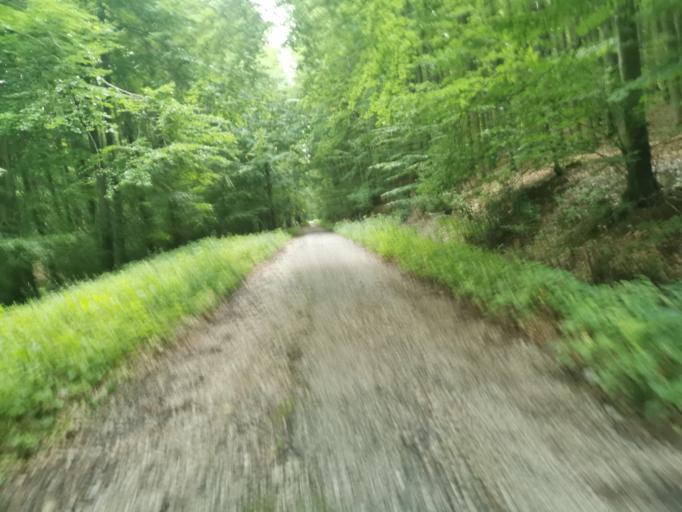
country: SK
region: Trenciansky
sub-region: Okres Myjava
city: Myjava
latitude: 48.8113
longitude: 17.6147
